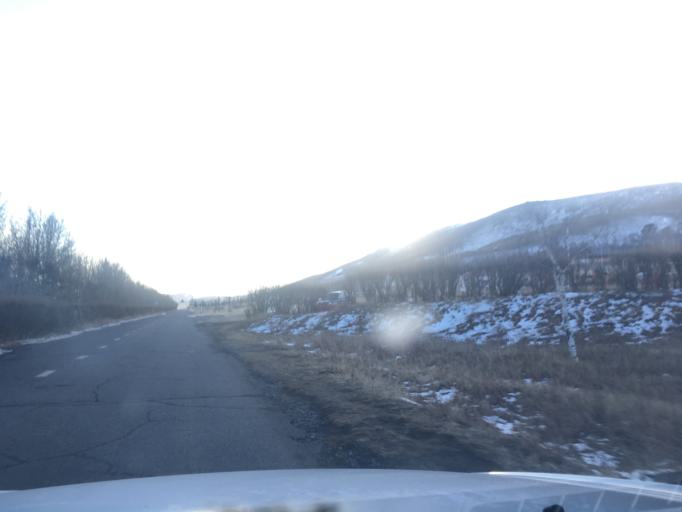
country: MN
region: Ulaanbaatar
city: Ulaanbaatar
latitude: 48.0160
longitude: 106.7307
